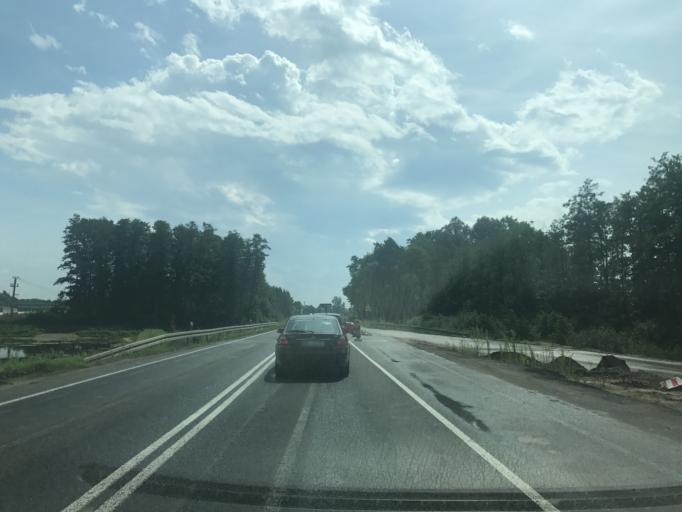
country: PL
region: Warmian-Masurian Voivodeship
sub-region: Powiat ostrodzki
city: Ostroda
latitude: 53.7242
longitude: 19.9463
